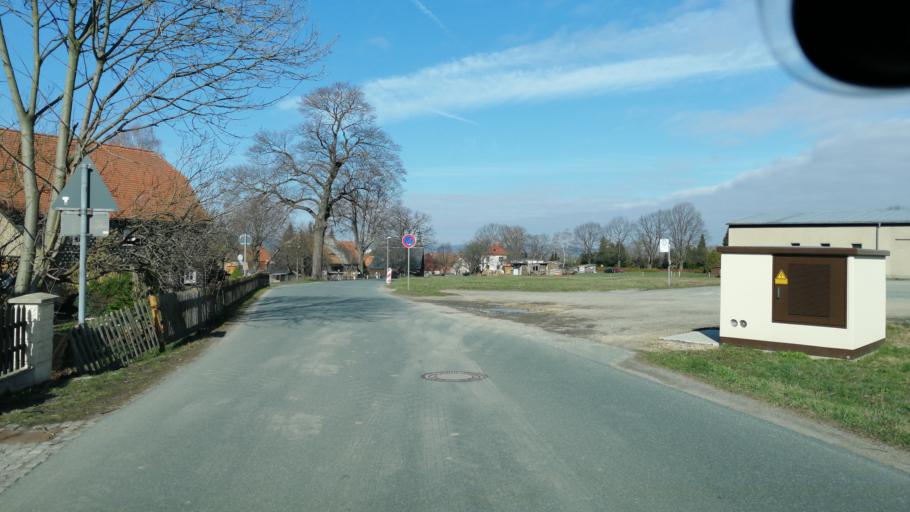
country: DE
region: Saxony
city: Niedercunnersdorf
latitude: 51.0331
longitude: 14.6740
